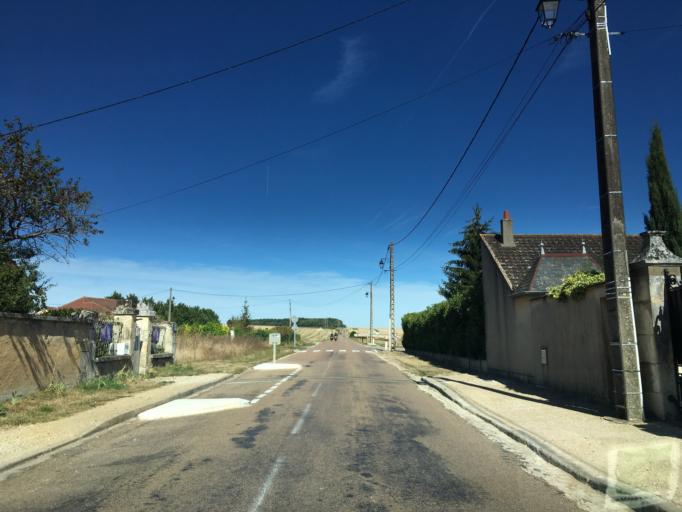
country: FR
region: Bourgogne
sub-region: Departement de l'Yonne
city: Vermenton
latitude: 47.6628
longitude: 3.6629
